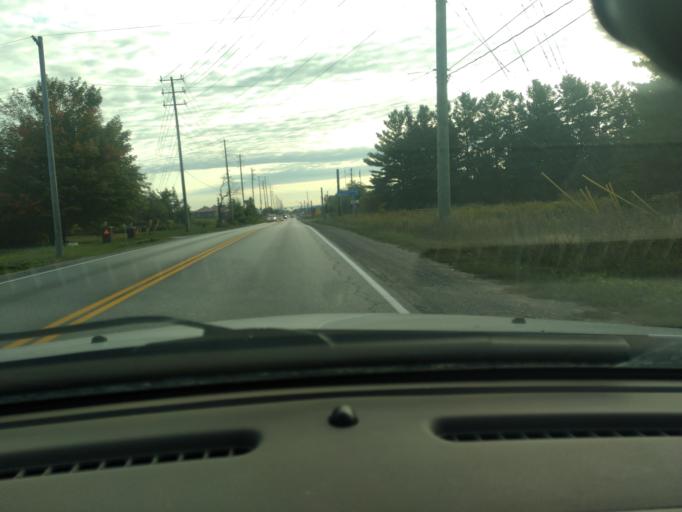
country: CA
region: Ontario
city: Innisfil
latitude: 44.3071
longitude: -79.5821
